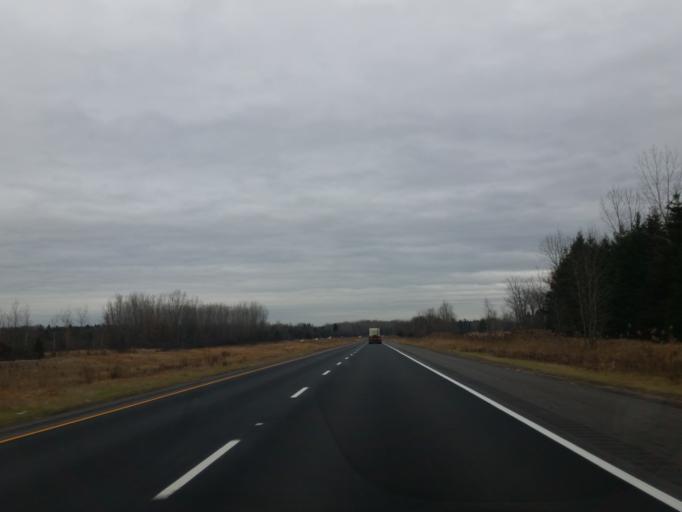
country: CA
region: Quebec
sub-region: Capitale-Nationale
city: Saint-Marc-des-Carrieres
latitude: 46.6042
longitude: -72.1219
